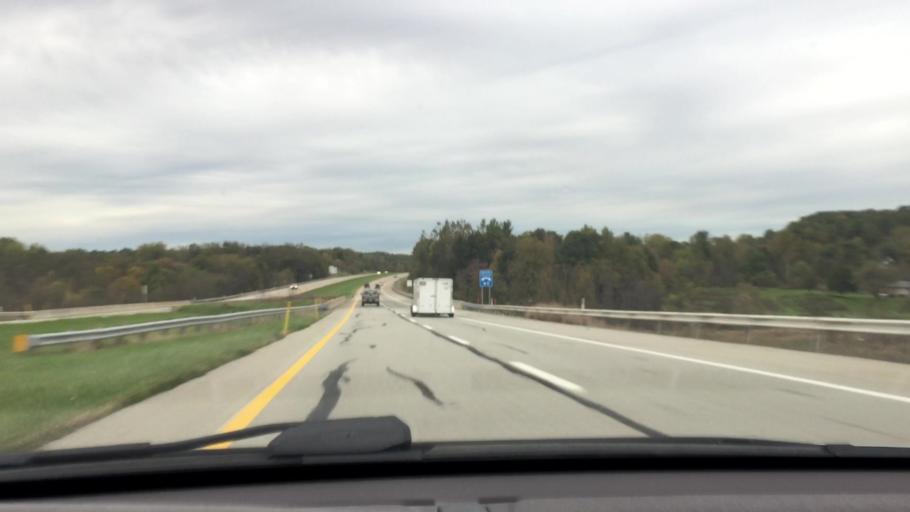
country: US
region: Pennsylvania
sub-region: Beaver County
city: Big Beaver
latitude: 40.8499
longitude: -80.3682
